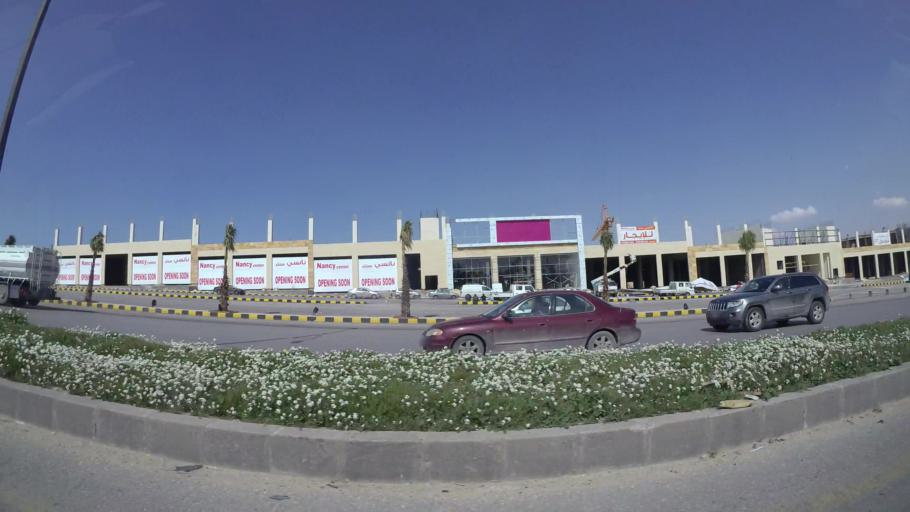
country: JO
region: Zarqa
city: Russeifa
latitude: 31.9977
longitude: 36.0106
